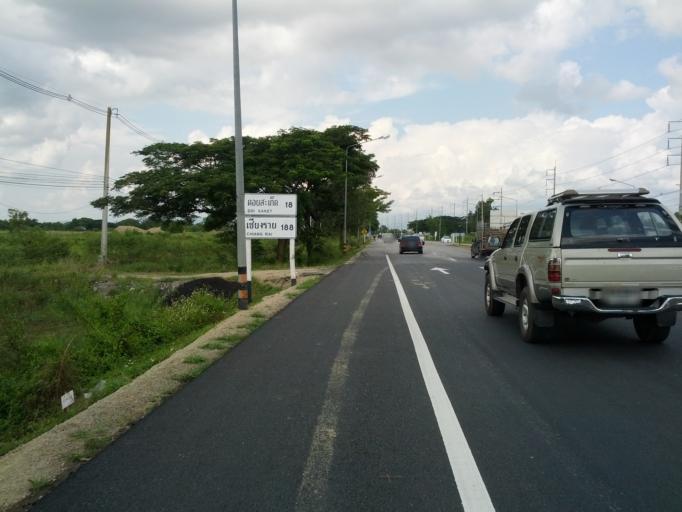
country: TH
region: Chiang Mai
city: San Kamphaeng
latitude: 18.7732
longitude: 99.0682
